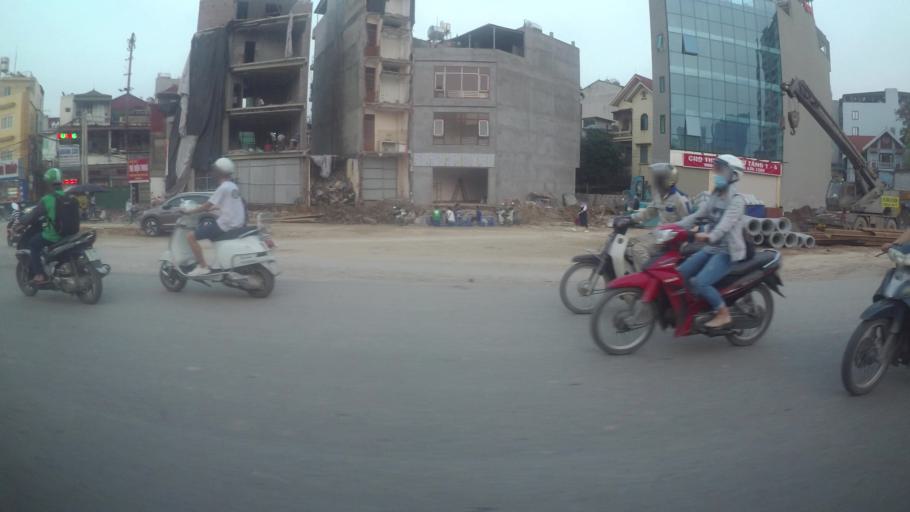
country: VN
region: Ha Noi
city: Cau Dien
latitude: 21.0583
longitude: 105.7830
